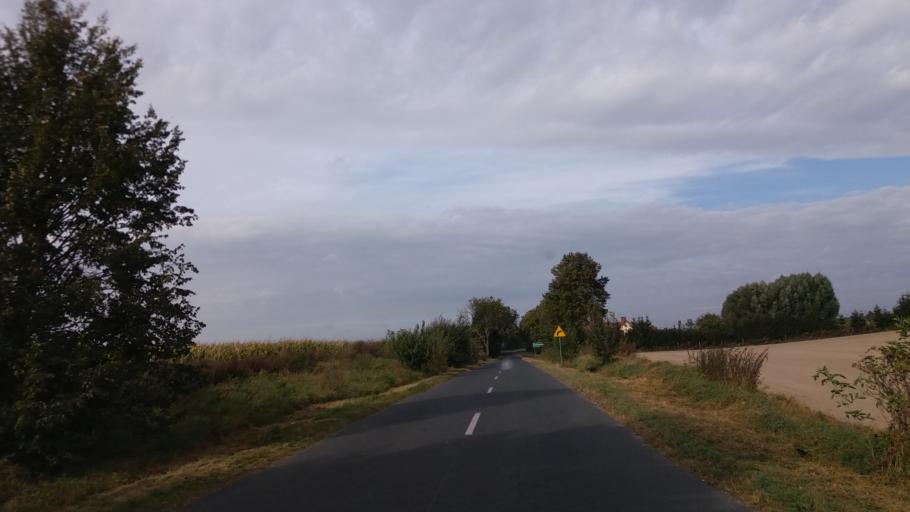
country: PL
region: West Pomeranian Voivodeship
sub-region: Powiat choszczenski
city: Krzecin
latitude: 53.0545
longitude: 15.4917
